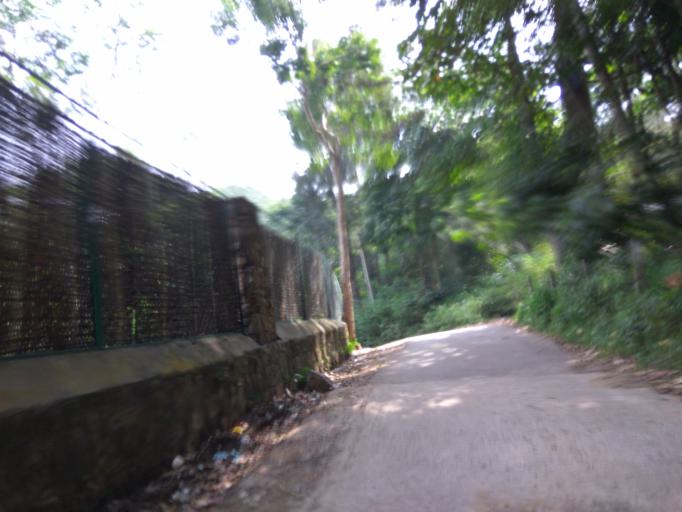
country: IN
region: Tamil Nadu
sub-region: Salem
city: Salem
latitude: 11.7932
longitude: 78.2018
